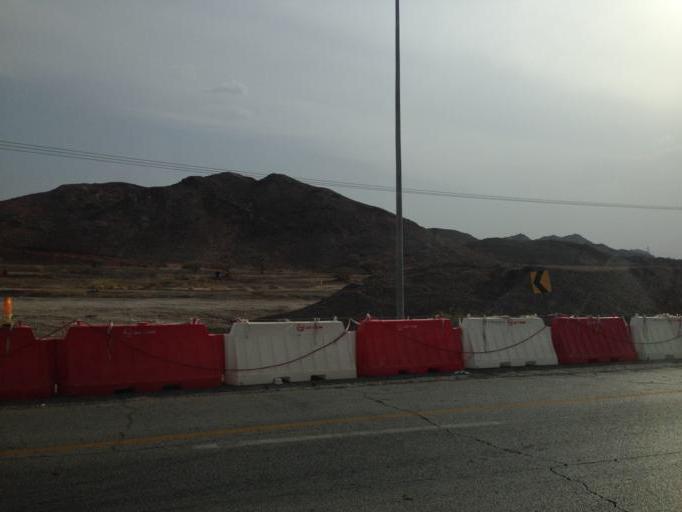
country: OM
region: Ash Sharqiyah
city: Al Qabil
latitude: 22.6426
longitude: 58.6364
